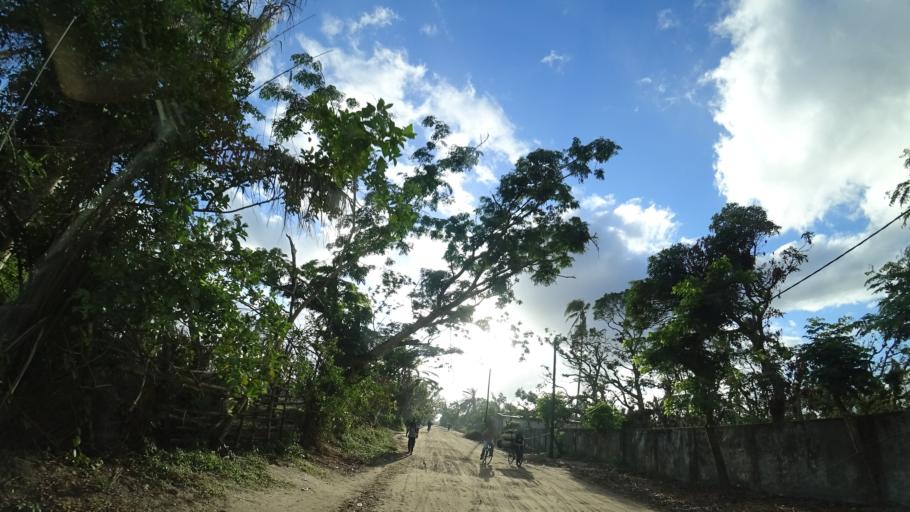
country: MZ
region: Sofala
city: Beira
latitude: -19.7667
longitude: 34.8939
